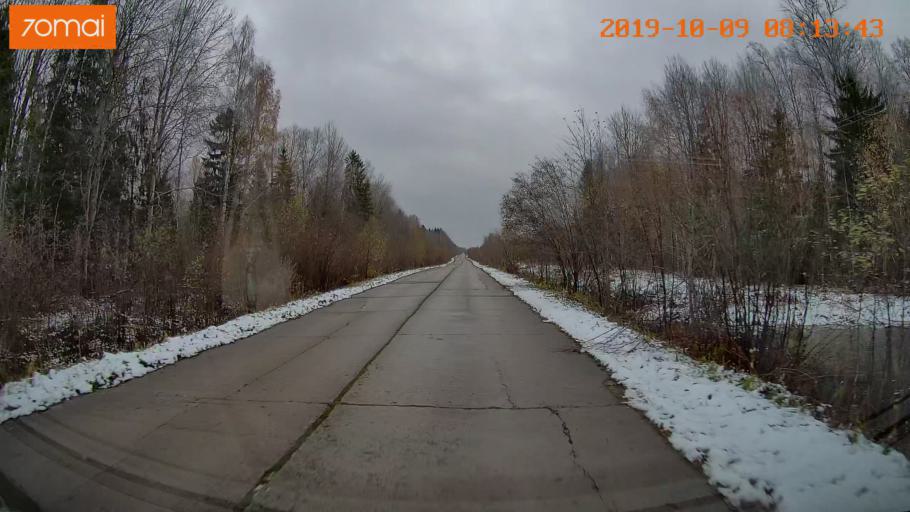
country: RU
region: Vologda
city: Gryazovets
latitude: 58.7248
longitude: 40.1440
